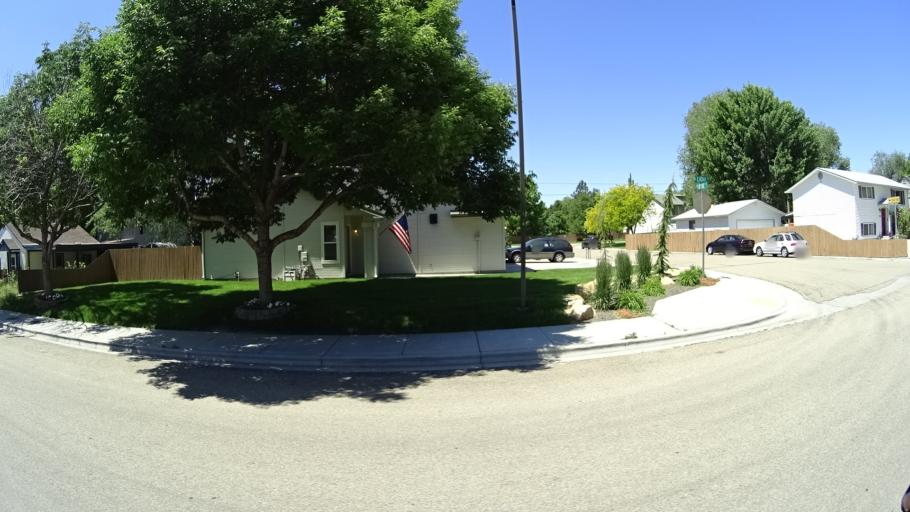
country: US
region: Idaho
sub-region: Ada County
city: Boise
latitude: 43.5855
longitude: -116.2286
